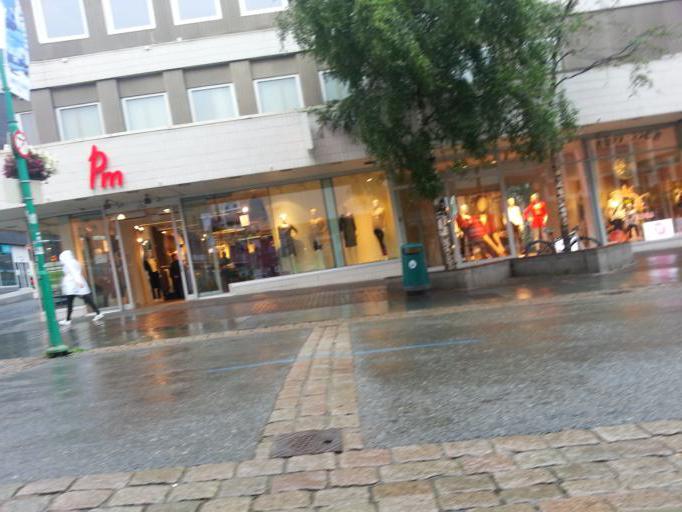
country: NO
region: Troms
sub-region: Tromso
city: Tromso
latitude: 69.6497
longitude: 18.9561
